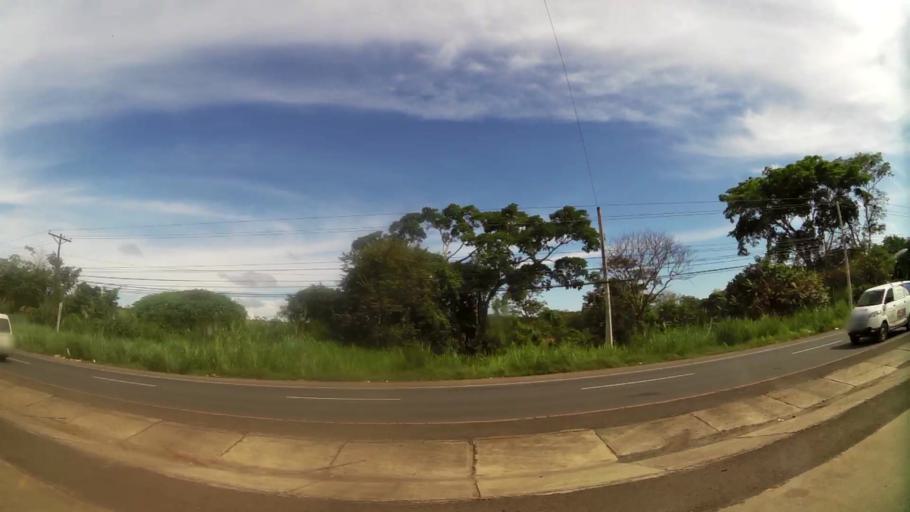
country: PA
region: Panama
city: La Chorrera
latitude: 8.8966
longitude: -79.7589
